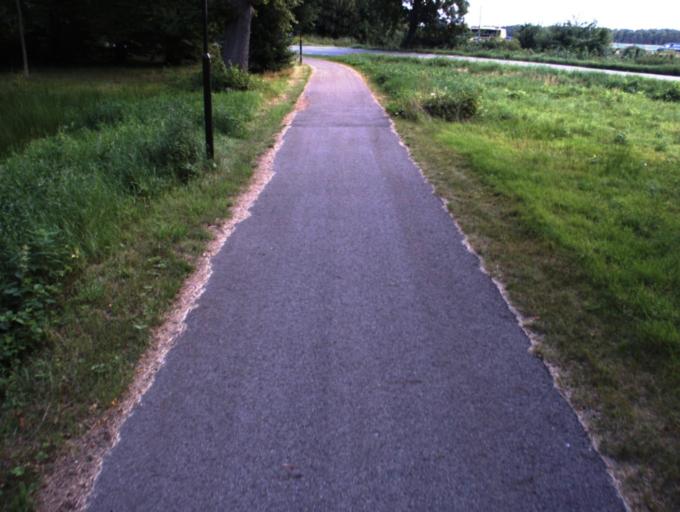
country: DK
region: Capital Region
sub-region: Helsingor Kommune
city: Helsingor
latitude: 56.1105
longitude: 12.6367
